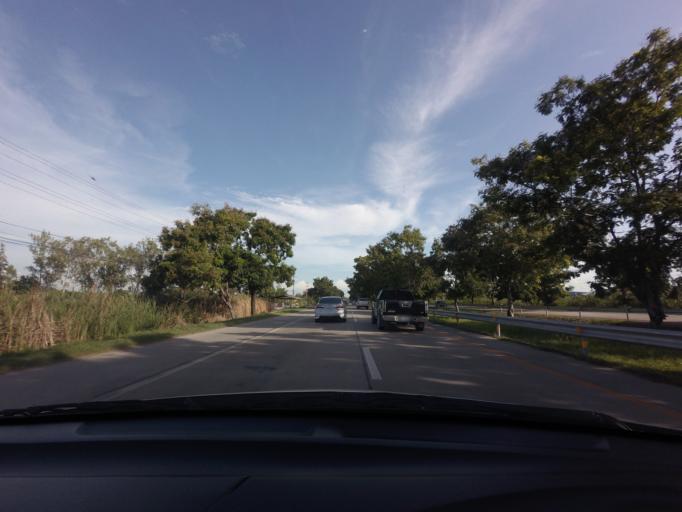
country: TH
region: Phra Nakhon Si Ayutthaya
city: Lat Bua Luang
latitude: 14.1953
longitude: 100.2927
